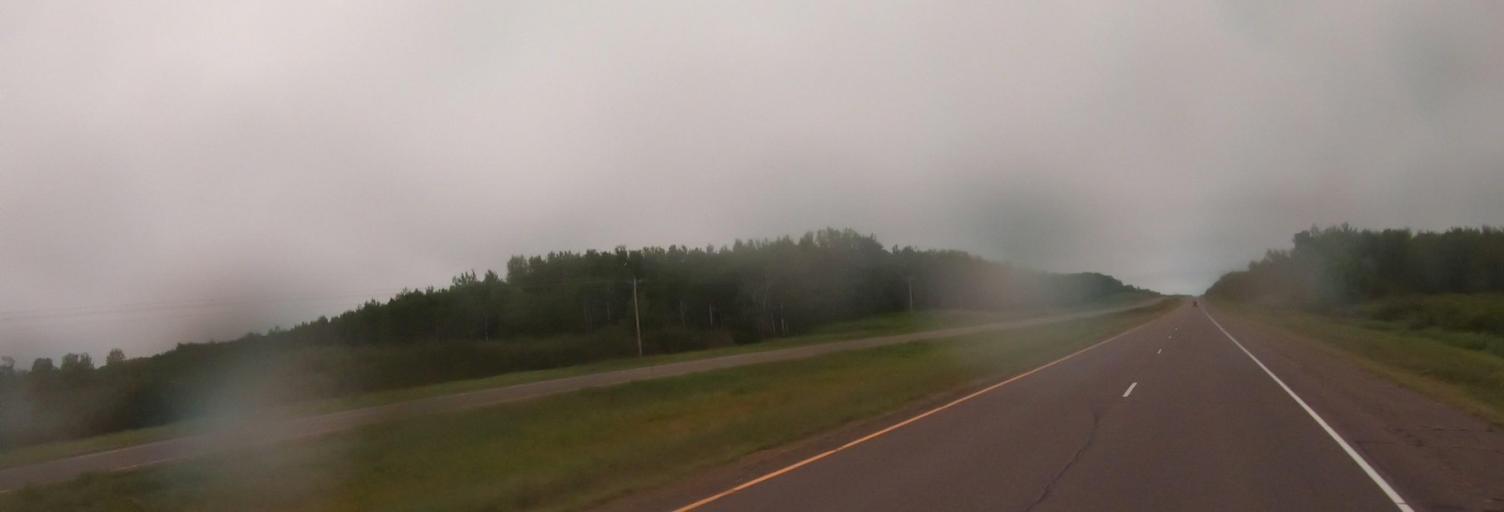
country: US
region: Minnesota
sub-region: Carlton County
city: Cloquet
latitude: 46.9258
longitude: -92.4707
